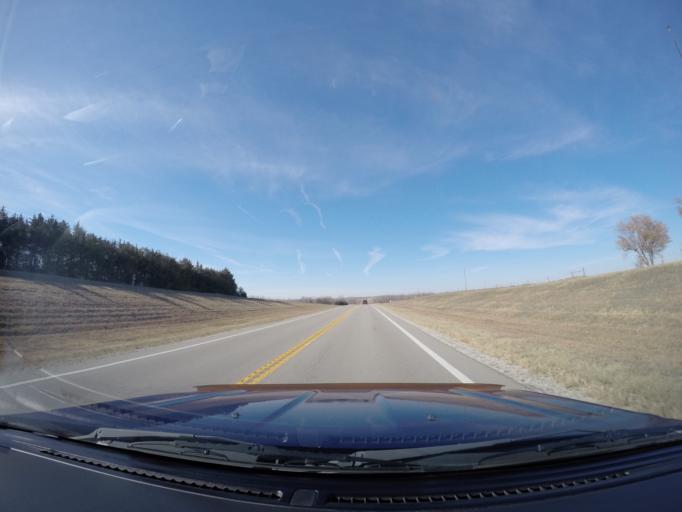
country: US
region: Kansas
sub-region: Cloud County
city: Concordia
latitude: 39.3647
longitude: -97.4377
